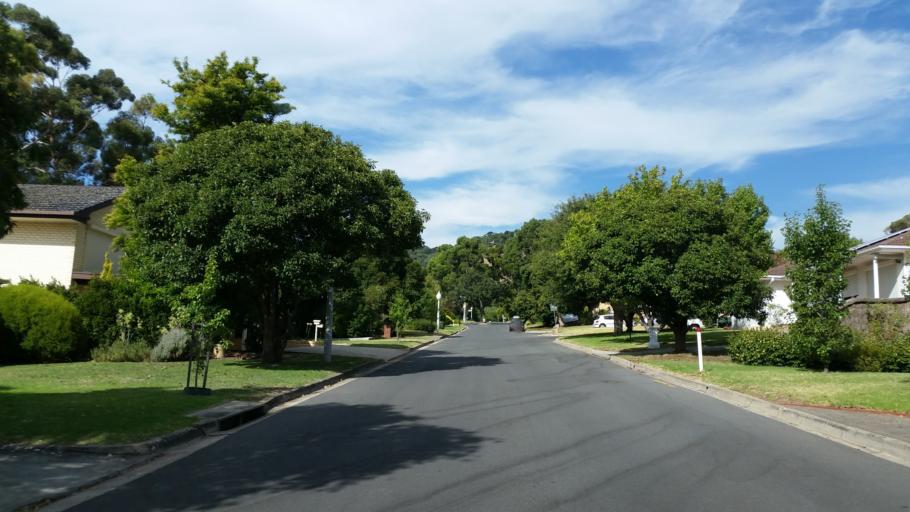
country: AU
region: South Australia
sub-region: Burnside
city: Mount Osmond
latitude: -34.9658
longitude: 138.6414
